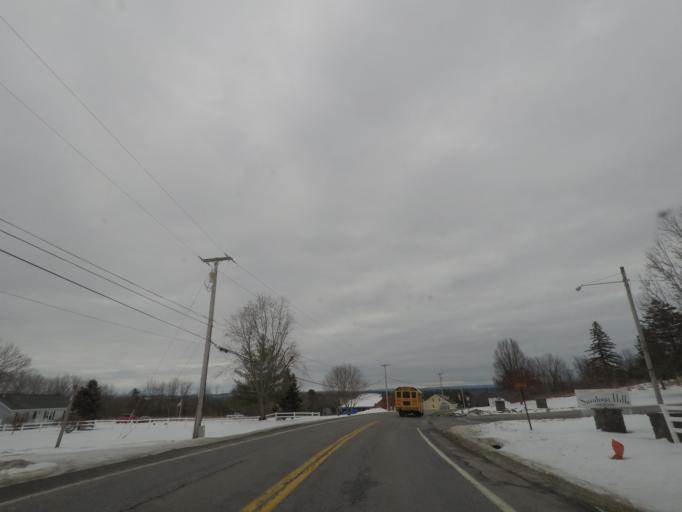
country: US
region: New York
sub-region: Saratoga County
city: Stillwater
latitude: 42.9531
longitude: -73.6675
